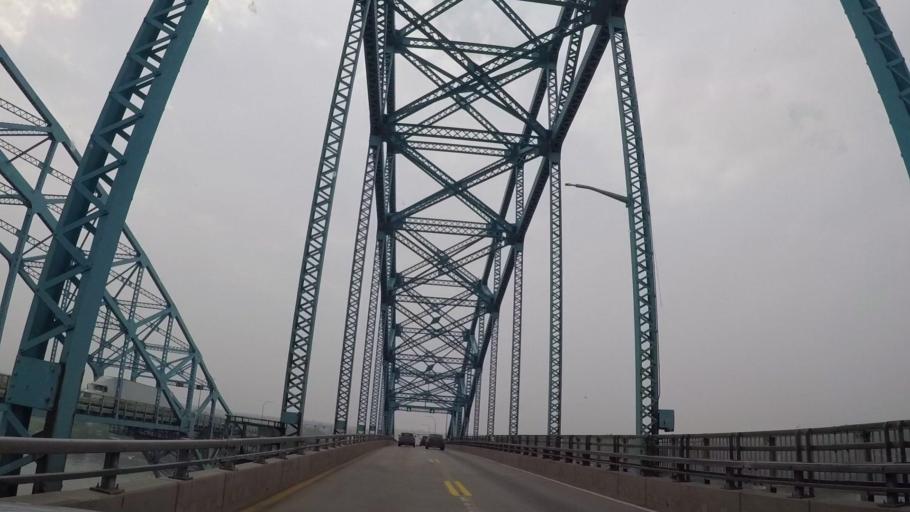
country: US
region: New York
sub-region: Erie County
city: Grandyle Village
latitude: 42.9986
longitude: -78.9366
